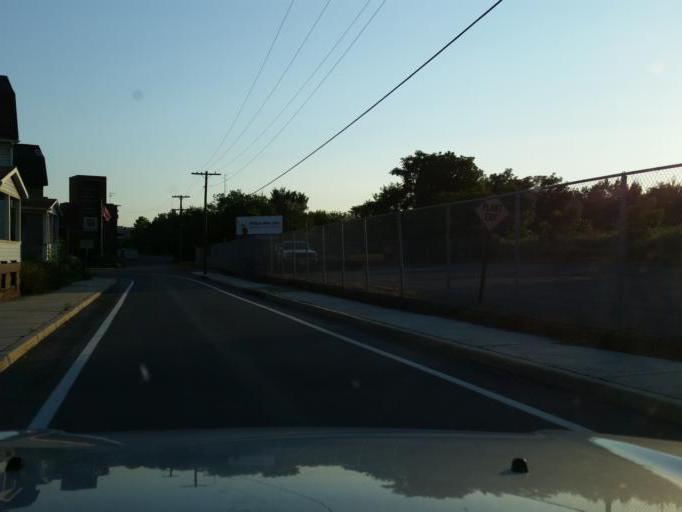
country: US
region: Pennsylvania
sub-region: Blair County
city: Altoona
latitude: 40.5231
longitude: -78.3876
